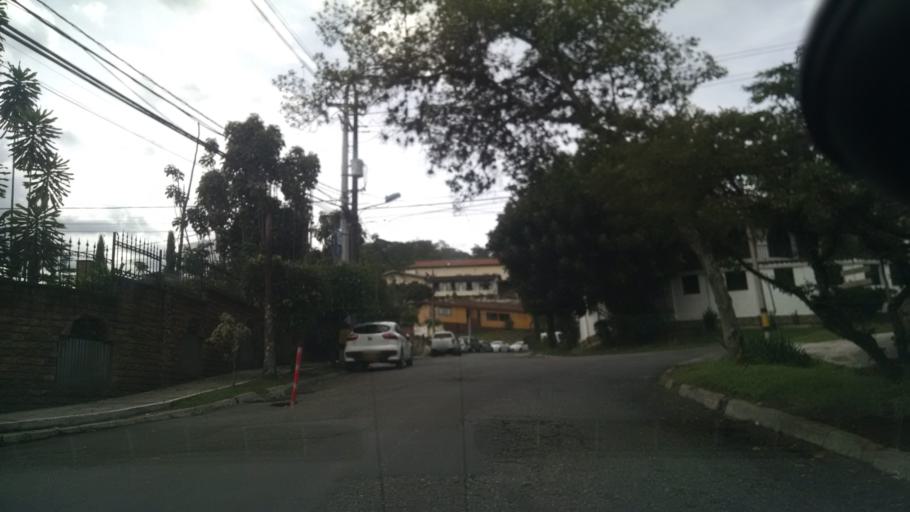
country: CO
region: Antioquia
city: Medellin
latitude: 6.2139
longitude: -75.5625
